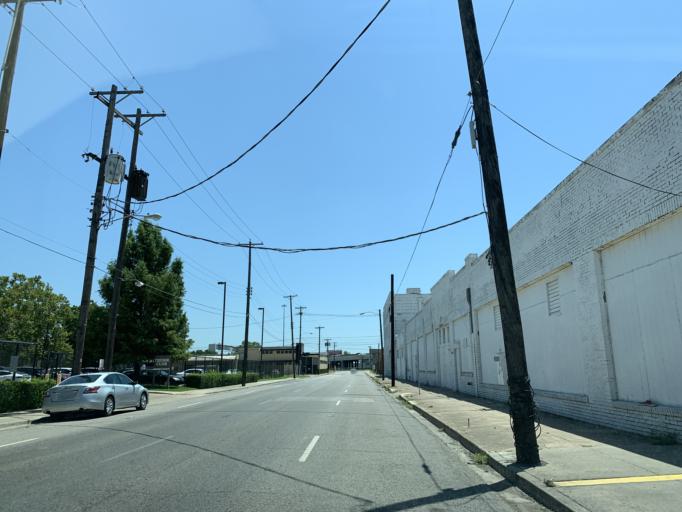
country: US
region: Texas
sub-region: Dallas County
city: Dallas
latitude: 32.7833
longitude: -96.7737
